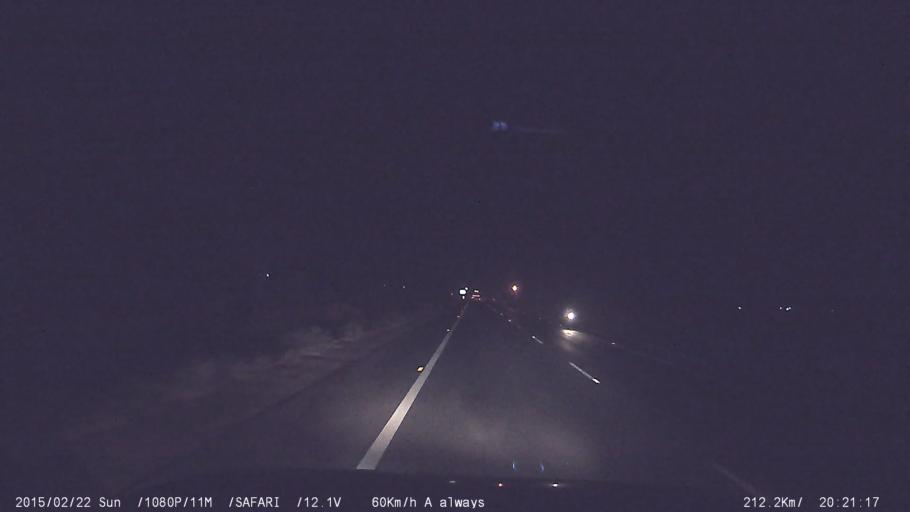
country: IN
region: Tamil Nadu
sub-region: Dindigul
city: Nilakottai
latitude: 10.2877
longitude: 77.8776
